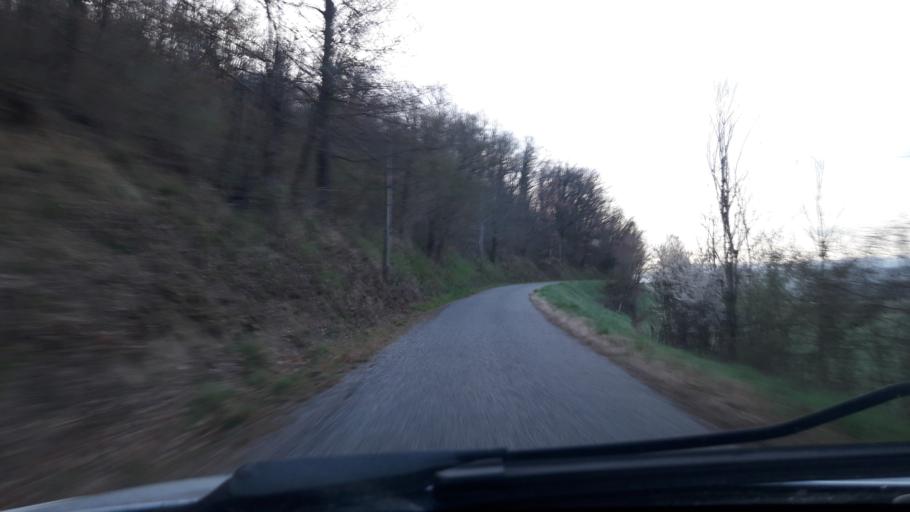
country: FR
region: Midi-Pyrenees
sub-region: Departement de la Haute-Garonne
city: Montesquieu-Volvestre
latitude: 43.1843
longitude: 1.2619
